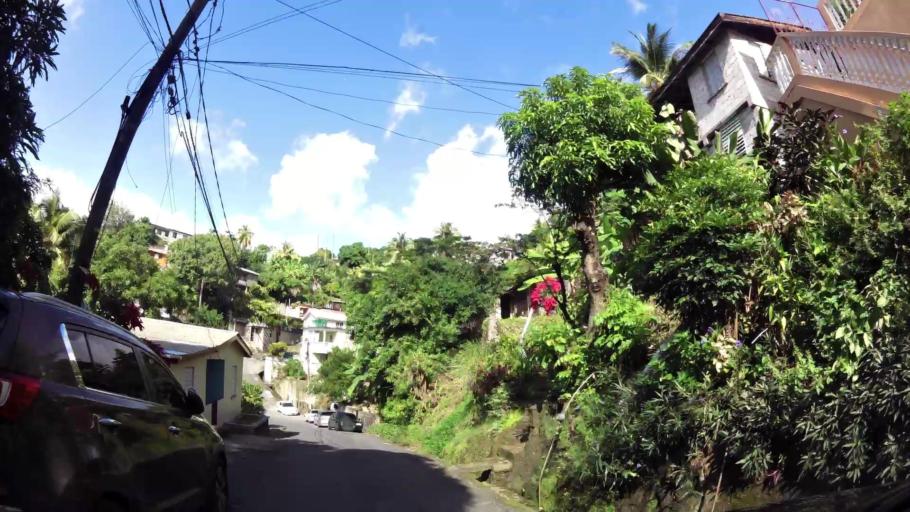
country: DM
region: Saint George
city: Roseau
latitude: 15.2907
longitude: -61.3760
